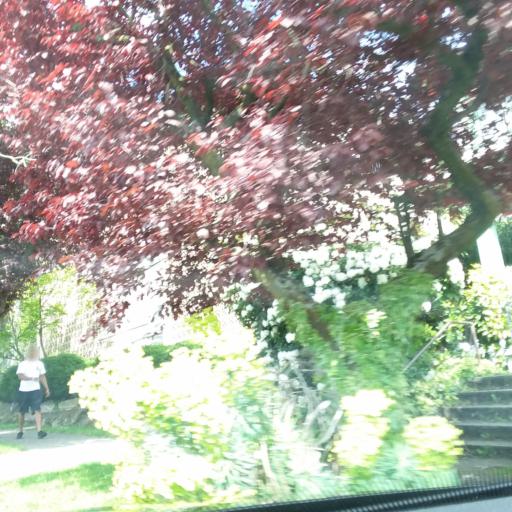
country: US
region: Washington
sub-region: King County
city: Seattle
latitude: 47.6587
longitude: -122.3155
